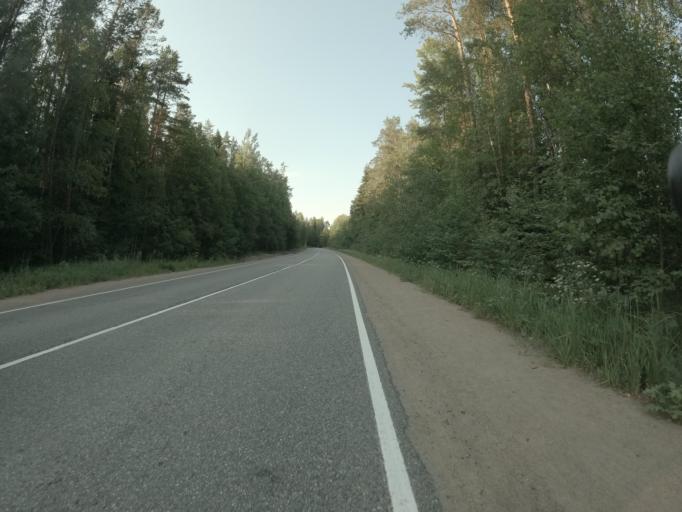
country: RU
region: Leningrad
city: Veshchevo
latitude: 60.4704
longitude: 29.2565
